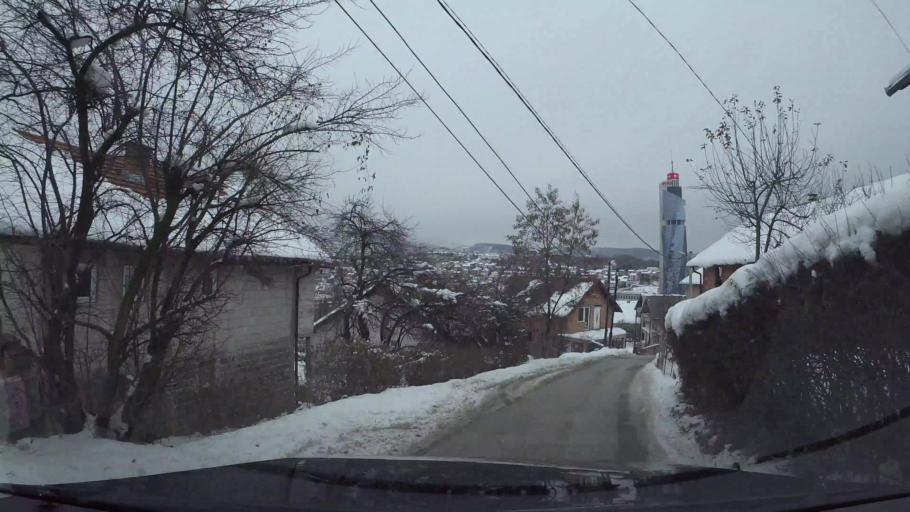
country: BA
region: Federation of Bosnia and Herzegovina
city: Kobilja Glava
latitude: 43.8617
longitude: 18.3965
